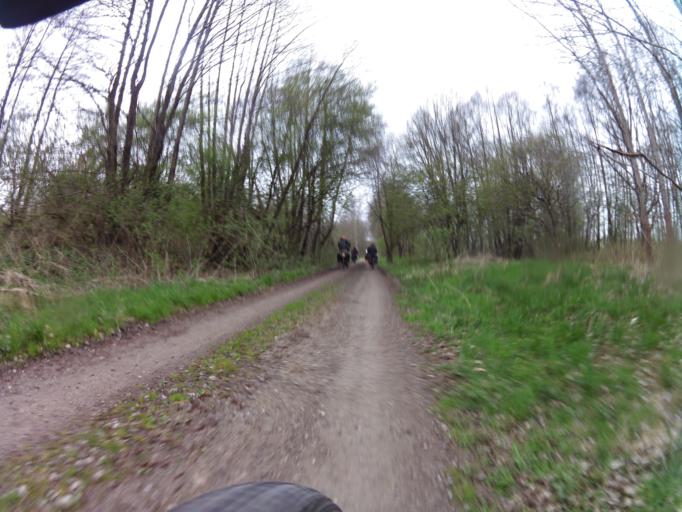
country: PL
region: West Pomeranian Voivodeship
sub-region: Powiat koszalinski
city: Bobolice
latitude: 54.0088
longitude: 16.6599
